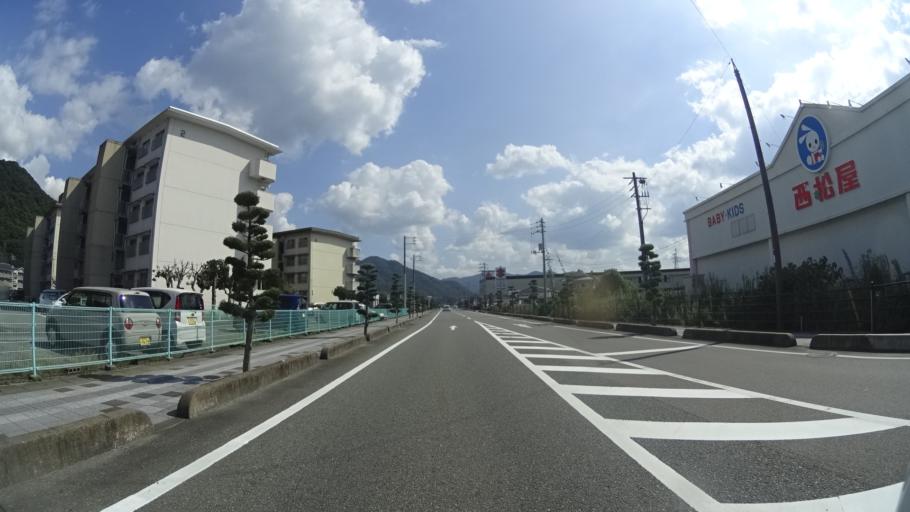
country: JP
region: Yamaguchi
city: Hagi
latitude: 34.4184
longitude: 131.4132
